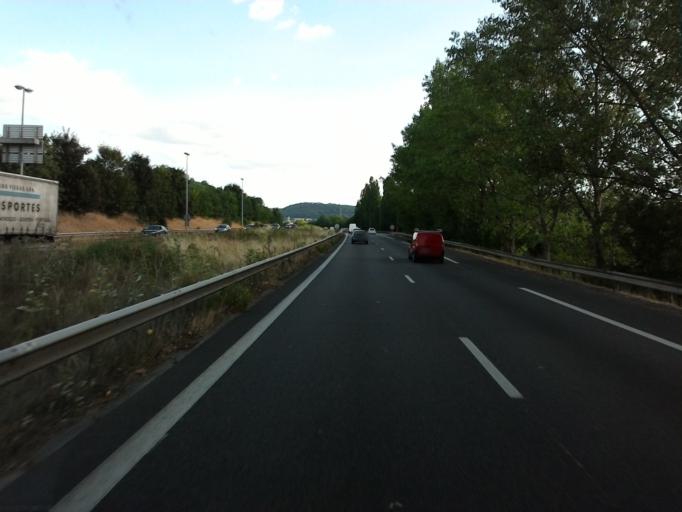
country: FR
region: Lorraine
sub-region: Departement de Meurthe-et-Moselle
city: Frouard
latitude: 48.7749
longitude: 6.1439
